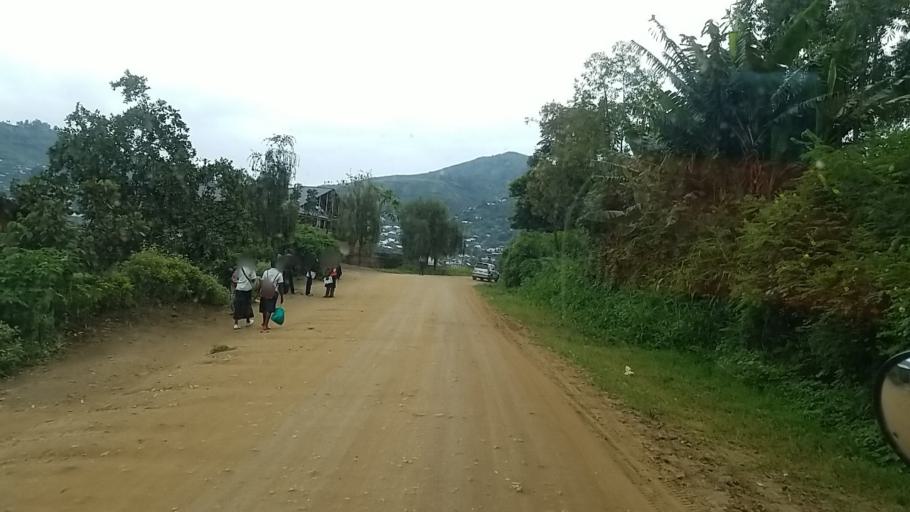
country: CD
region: Nord Kivu
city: Sake
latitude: -1.7036
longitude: 29.0175
